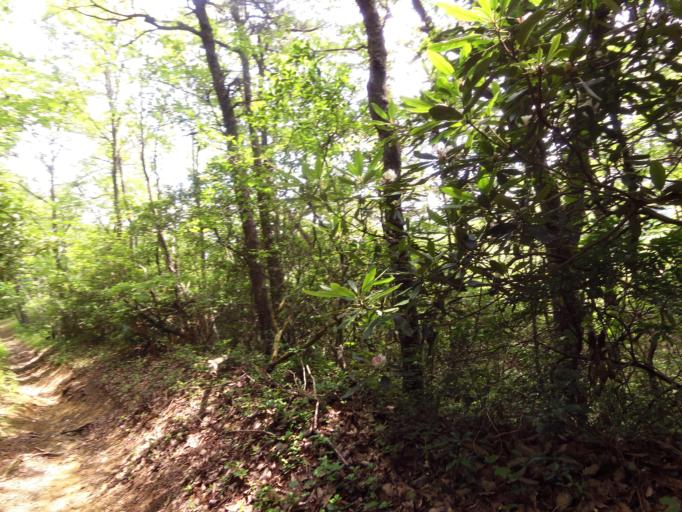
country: US
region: Tennessee
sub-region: Blount County
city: Wildwood
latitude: 35.5907
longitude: -83.7341
